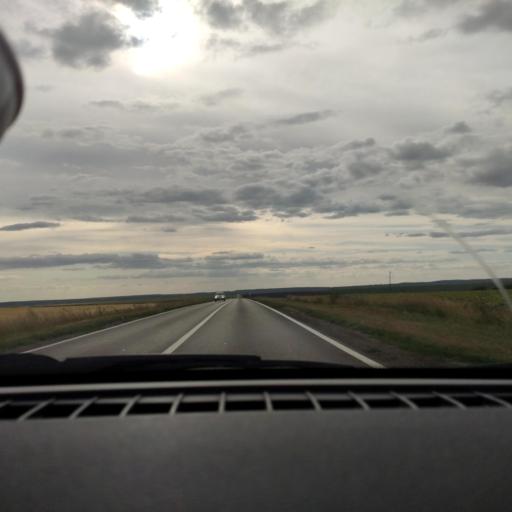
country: RU
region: Samara
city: Georgiyevka
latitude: 53.4174
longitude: 50.9233
